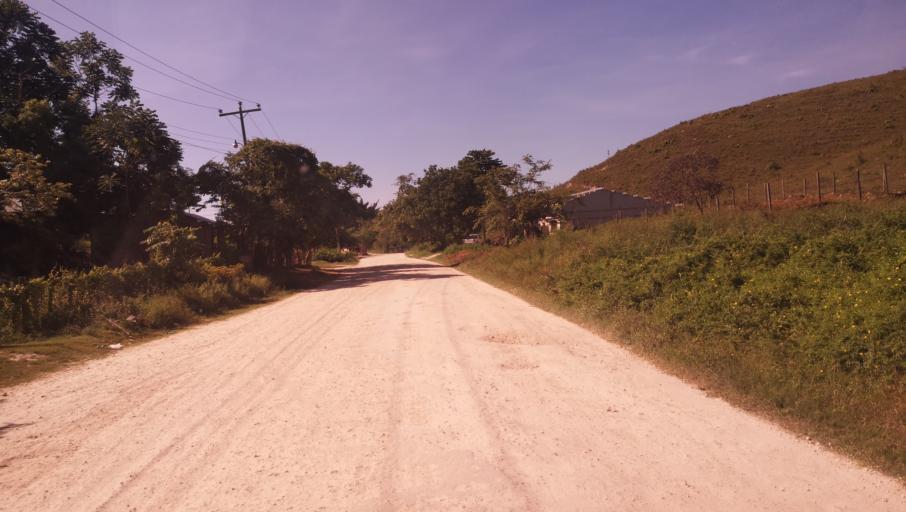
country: GT
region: Peten
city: Dolores
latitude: 16.7246
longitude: -89.3789
